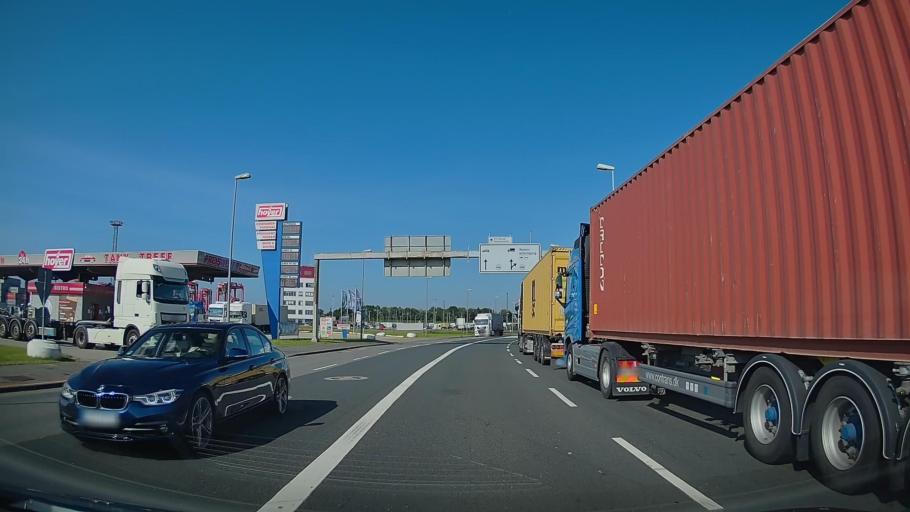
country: DE
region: Bremen
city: Bremerhaven
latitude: 53.5923
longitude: 8.5392
